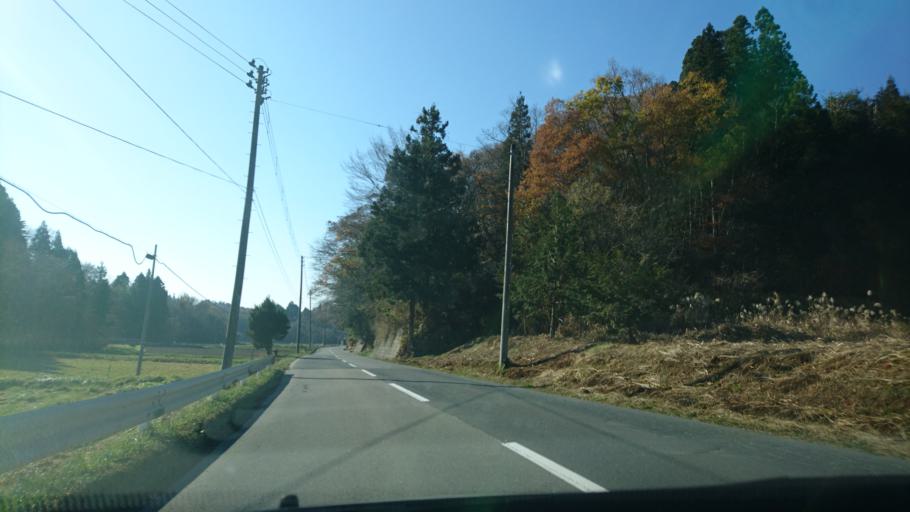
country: JP
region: Iwate
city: Ichinoseki
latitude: 38.9034
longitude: 141.4000
